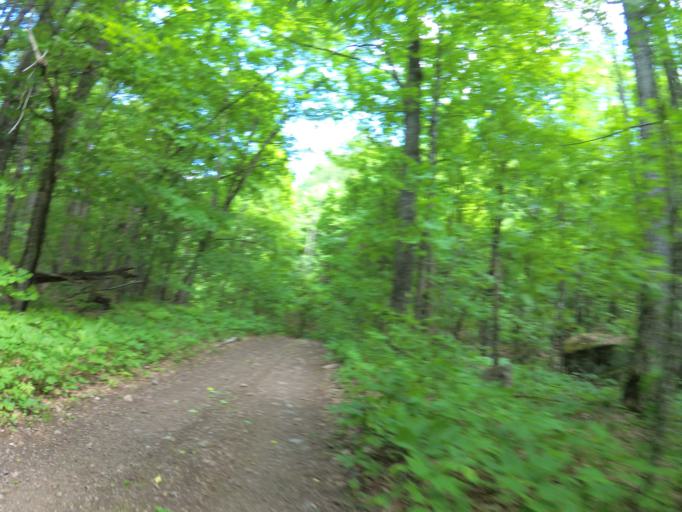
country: CA
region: Ontario
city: Renfrew
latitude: 45.0538
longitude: -76.8621
